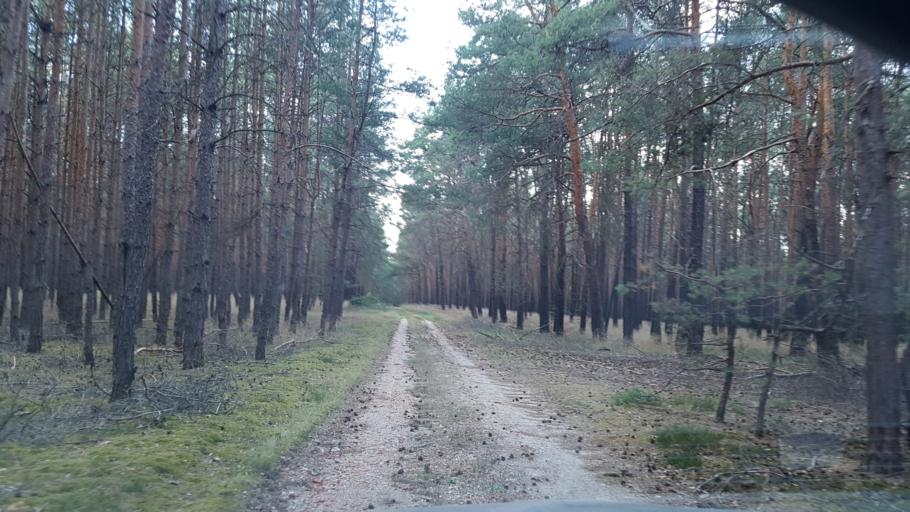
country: DE
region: Brandenburg
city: Schilda
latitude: 51.6171
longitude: 13.4009
